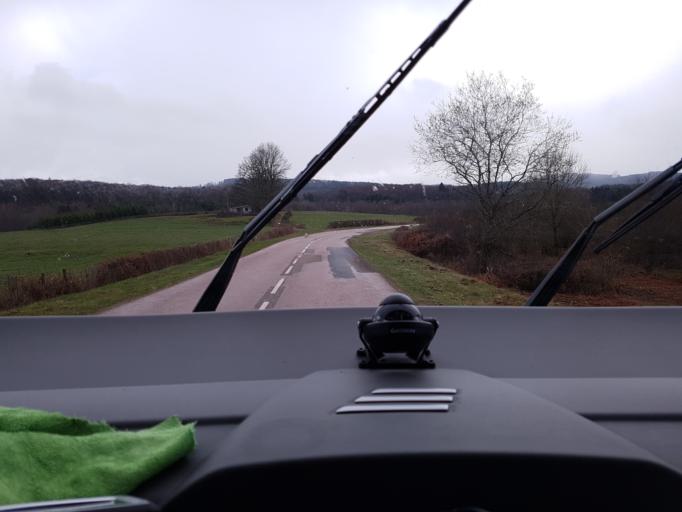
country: FR
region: Bourgogne
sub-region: Departement de la Cote-d'Or
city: Saulieu
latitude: 47.2622
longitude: 4.0282
